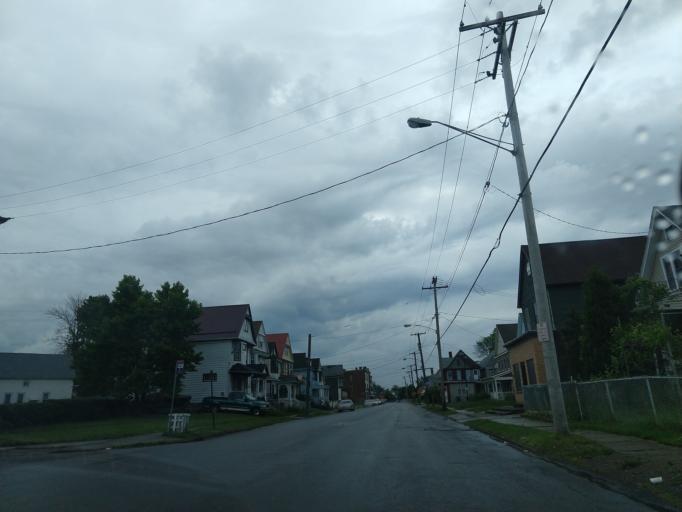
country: US
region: New York
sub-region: Erie County
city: Buffalo
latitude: 42.9128
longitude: -78.8924
